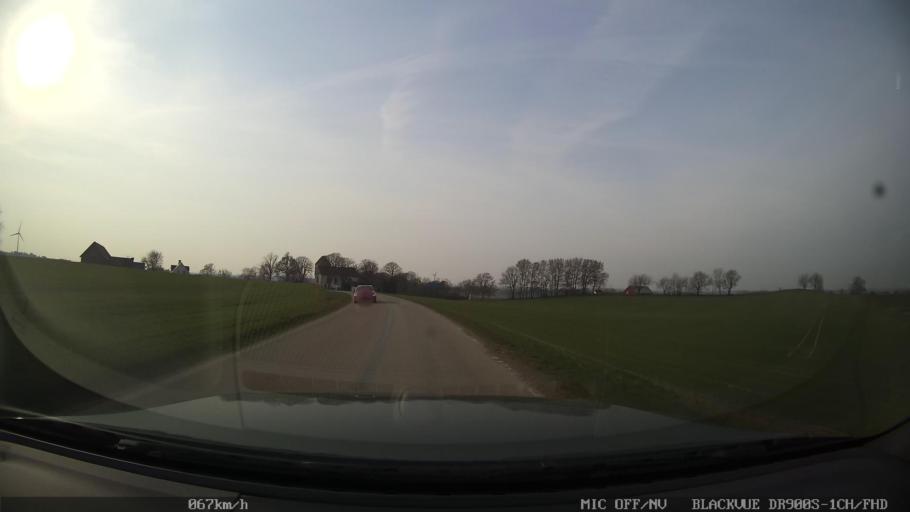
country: SE
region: Skane
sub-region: Ystads Kommun
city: Ystad
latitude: 55.4696
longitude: 13.8048
